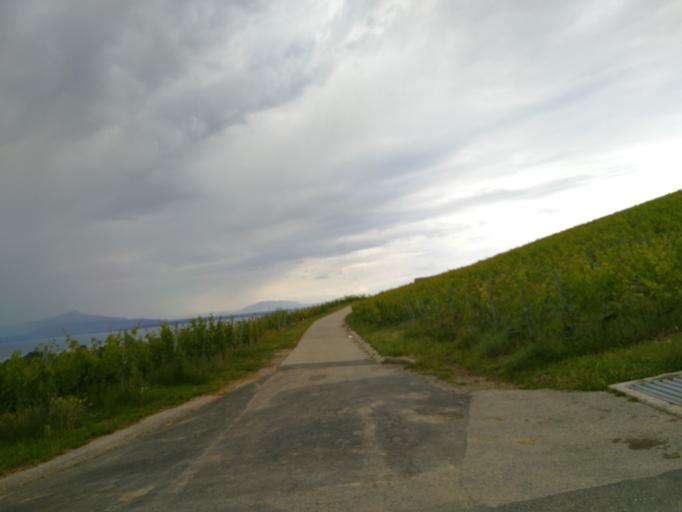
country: CH
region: Vaud
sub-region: Nyon District
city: Perroy
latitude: 46.4803
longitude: 6.3673
